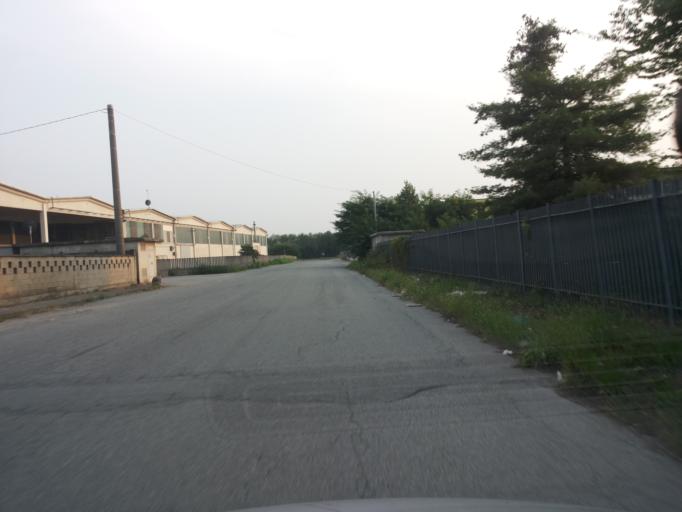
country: IT
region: Piedmont
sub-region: Provincia di Biella
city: Cavaglia
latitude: 45.3833
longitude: 8.1212
